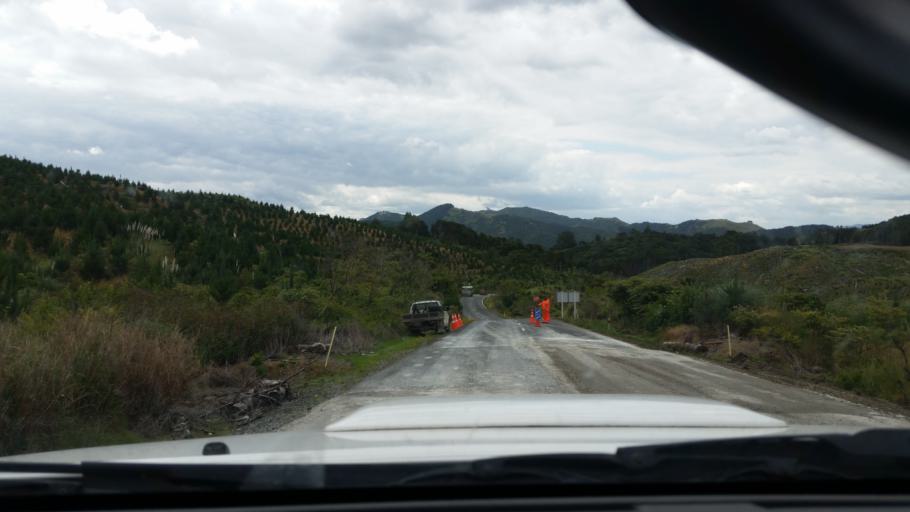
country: NZ
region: Northland
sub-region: Kaipara District
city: Dargaville
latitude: -35.7230
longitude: 173.8589
